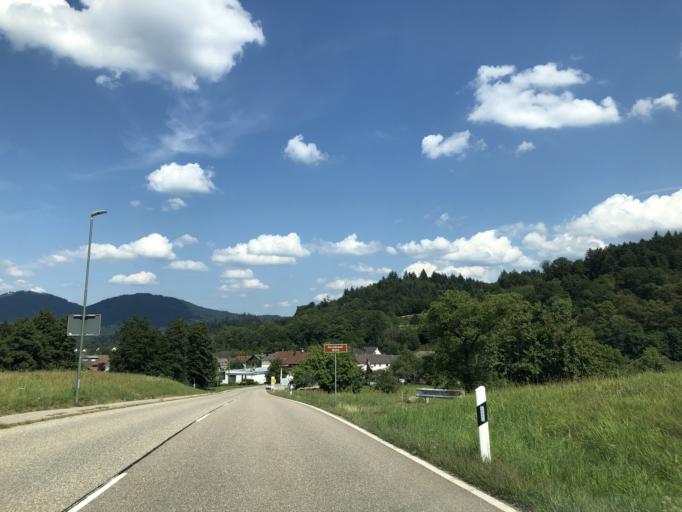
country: DE
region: Baden-Wuerttemberg
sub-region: Karlsruhe Region
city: Baden-Baden
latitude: 48.7235
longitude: 8.2437
